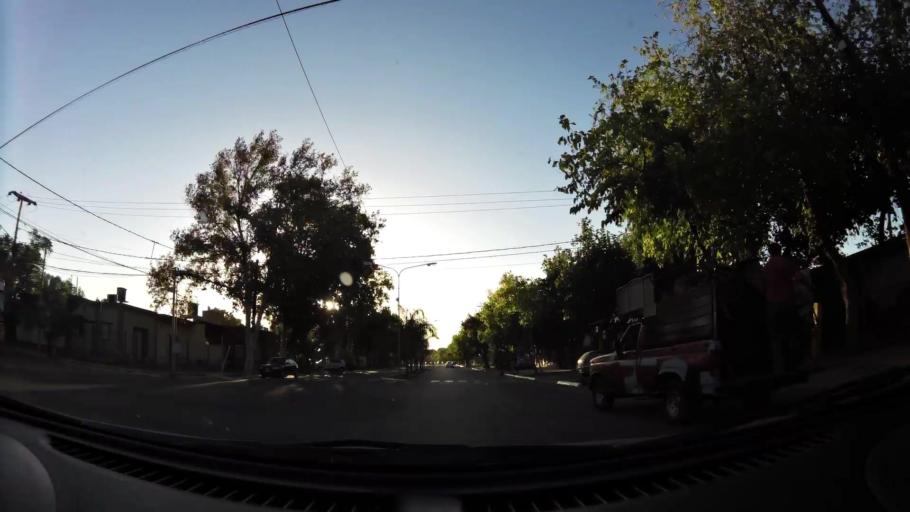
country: AR
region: San Juan
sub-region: Departamento de Santa Lucia
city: Santa Lucia
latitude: -31.5423
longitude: -68.4912
